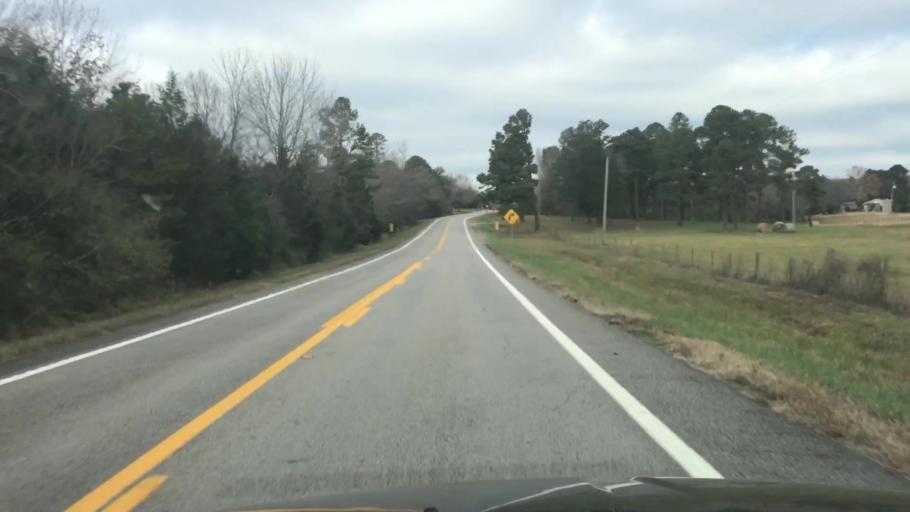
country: US
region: Arkansas
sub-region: Montgomery County
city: Mount Ida
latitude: 34.6503
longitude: -93.7529
